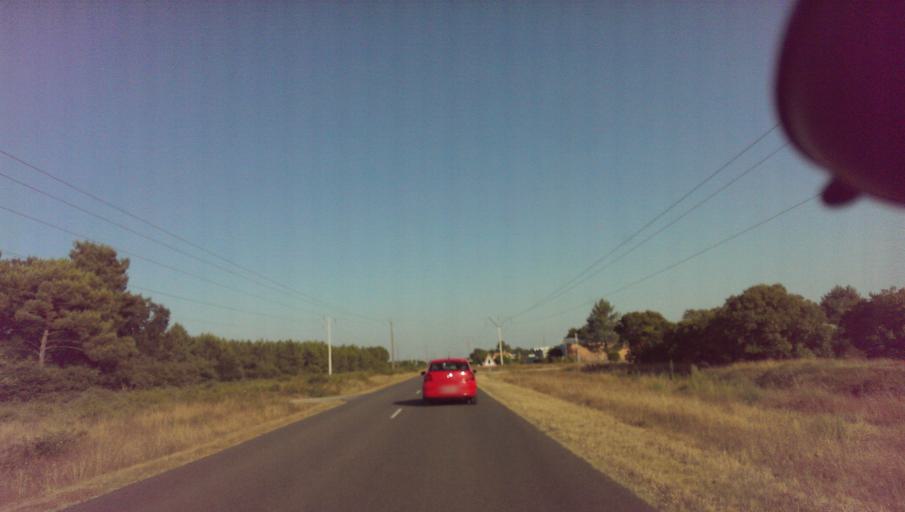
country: FR
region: Aquitaine
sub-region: Departement des Landes
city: Mimizan
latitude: 44.1905
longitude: -1.2148
